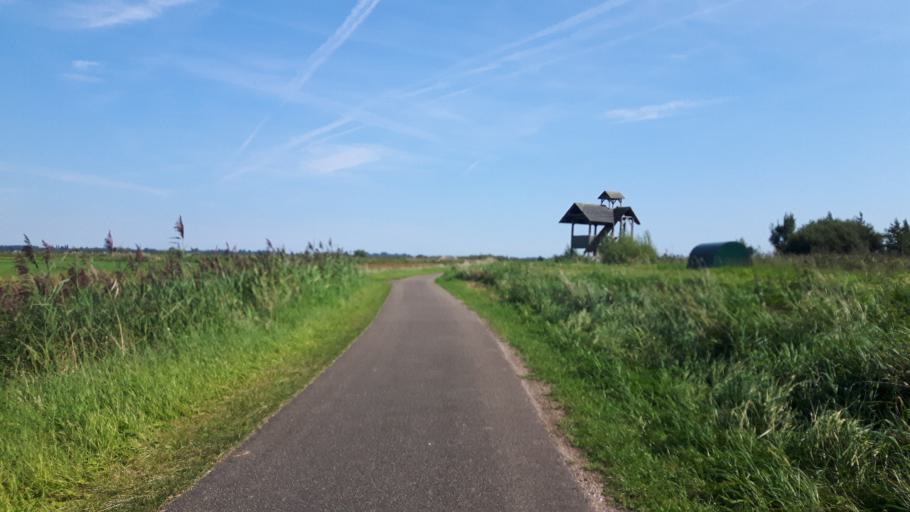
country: NL
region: Drenthe
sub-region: Gemeente Tynaarlo
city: Zuidlaren
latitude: 53.1314
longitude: 6.6810
